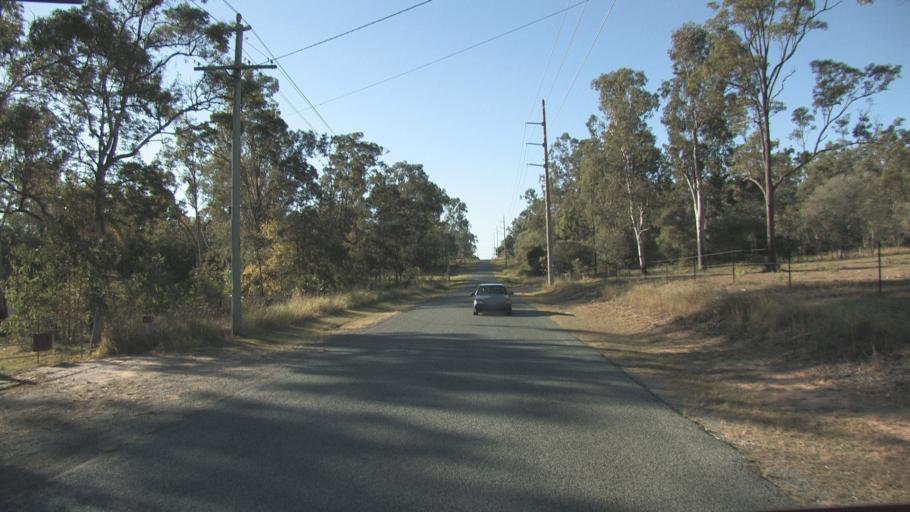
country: AU
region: Queensland
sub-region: Logan
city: North Maclean
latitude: -27.8022
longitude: 153.0409
